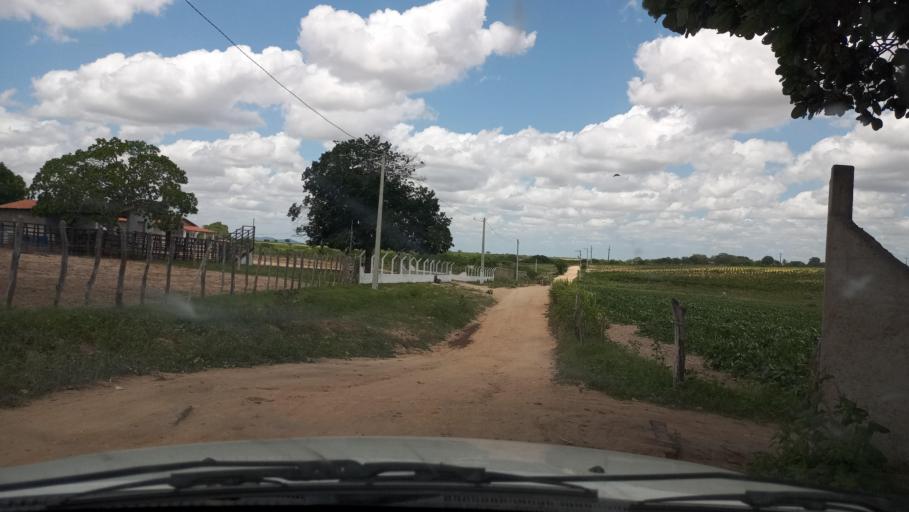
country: BR
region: Rio Grande do Norte
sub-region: Sao Jose Do Campestre
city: Sao Jose do Campestre
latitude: -6.4278
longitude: -35.6302
